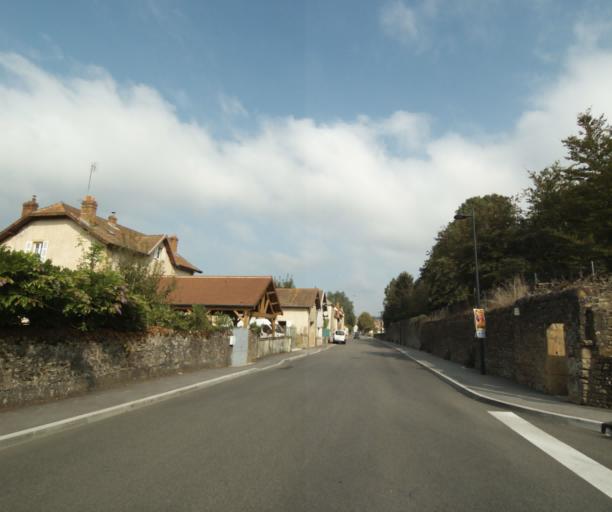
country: FR
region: Bourgogne
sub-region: Departement de Saone-et-Loire
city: Charolles
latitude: 46.4299
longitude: 4.2761
